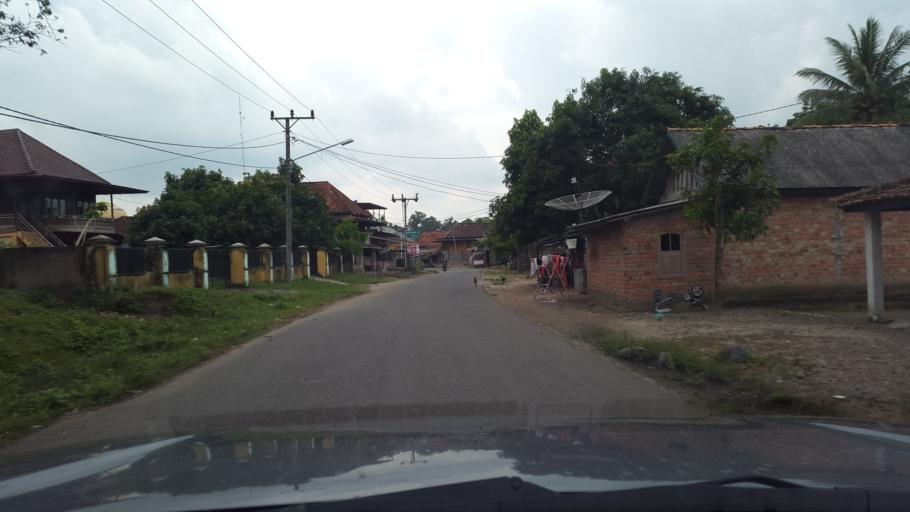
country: ID
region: South Sumatra
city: Gunungmenang
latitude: -3.1767
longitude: 104.0343
